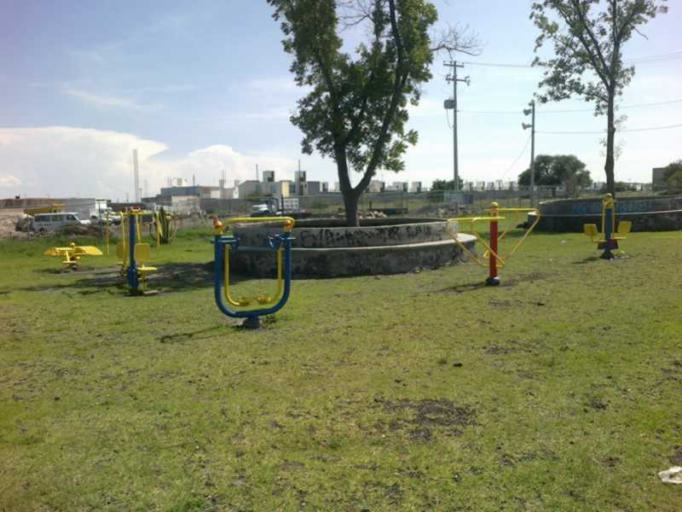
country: MX
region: Queretaro
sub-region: Queretaro
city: Sergio Villasenor
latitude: 20.6414
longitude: -100.4092
